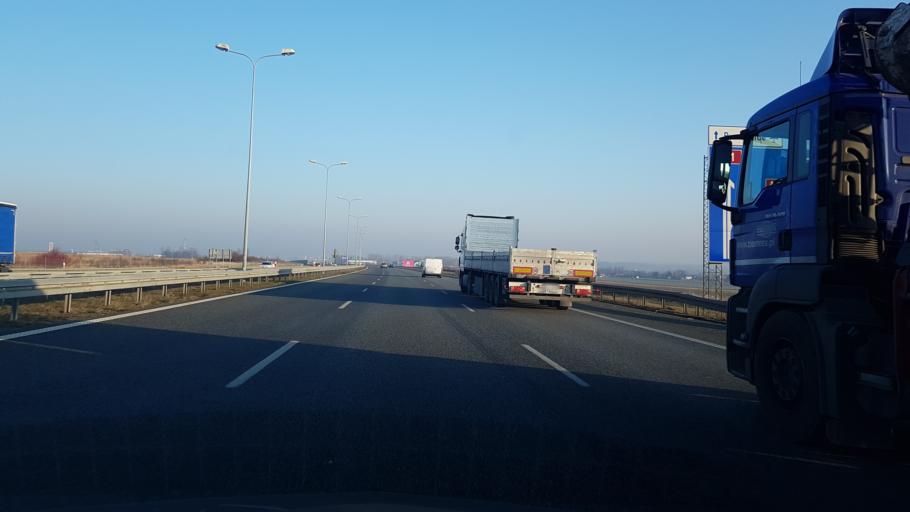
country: PL
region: Silesian Voivodeship
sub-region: Powiat gliwicki
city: Gieraltowice
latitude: 50.2425
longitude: 18.7114
